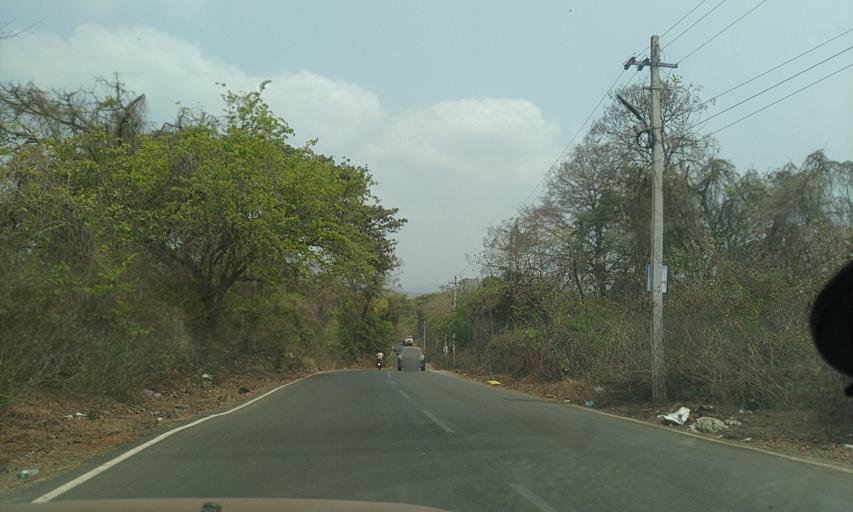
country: IN
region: Goa
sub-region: North Goa
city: Goa Velha
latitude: 15.4921
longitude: 73.9110
